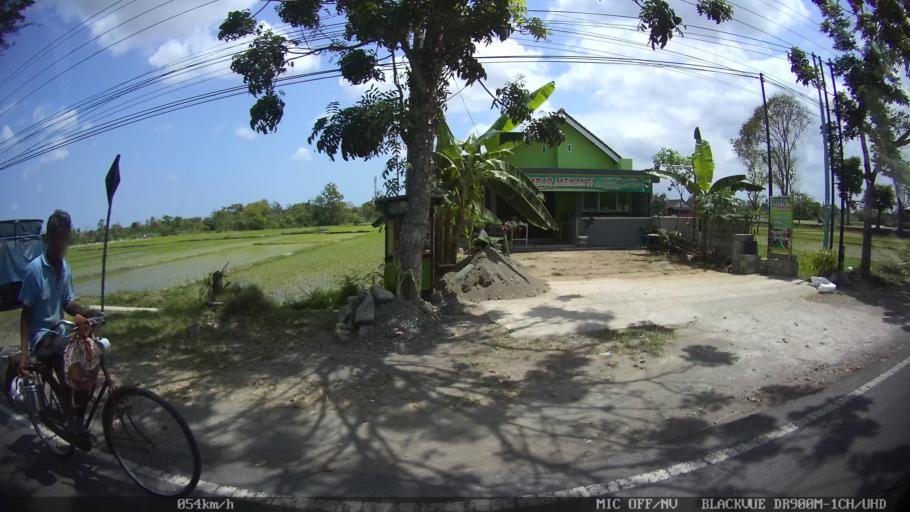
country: ID
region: Daerah Istimewa Yogyakarta
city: Bantul
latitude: -7.8997
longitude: 110.3460
